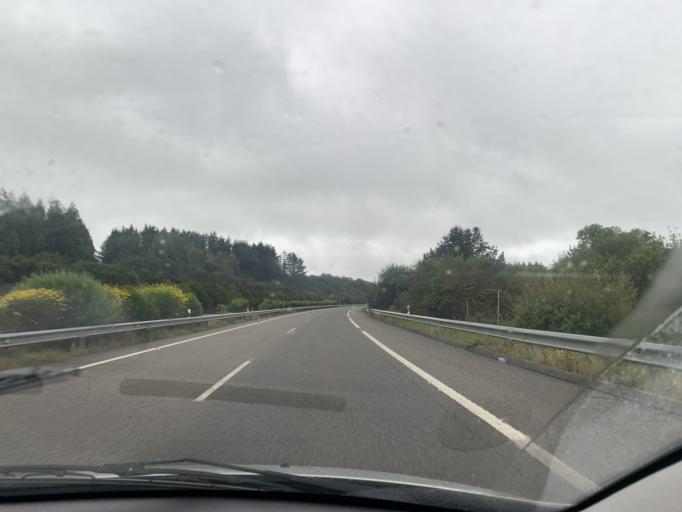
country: ES
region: Galicia
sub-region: Provincia de Lugo
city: Abadin
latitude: 43.3481
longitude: -7.5043
